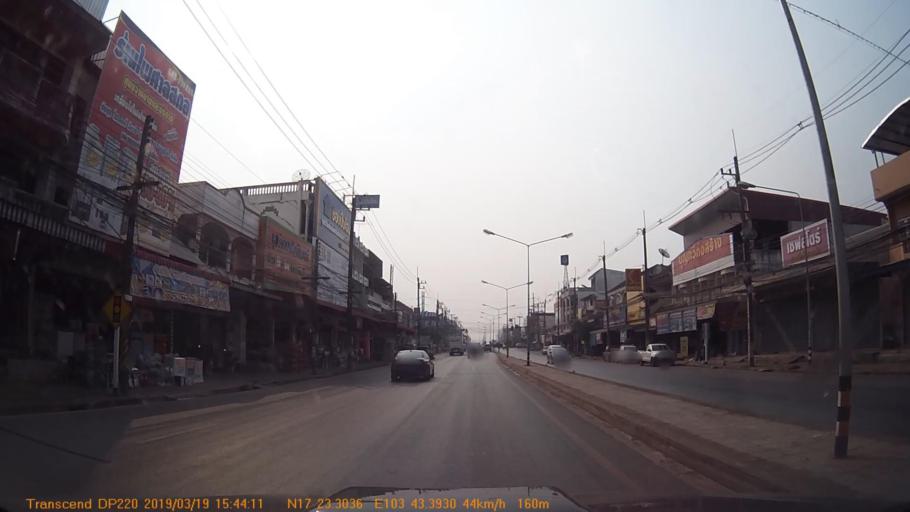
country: TH
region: Sakon Nakhon
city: Phang Khon
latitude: 17.3884
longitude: 103.7231
